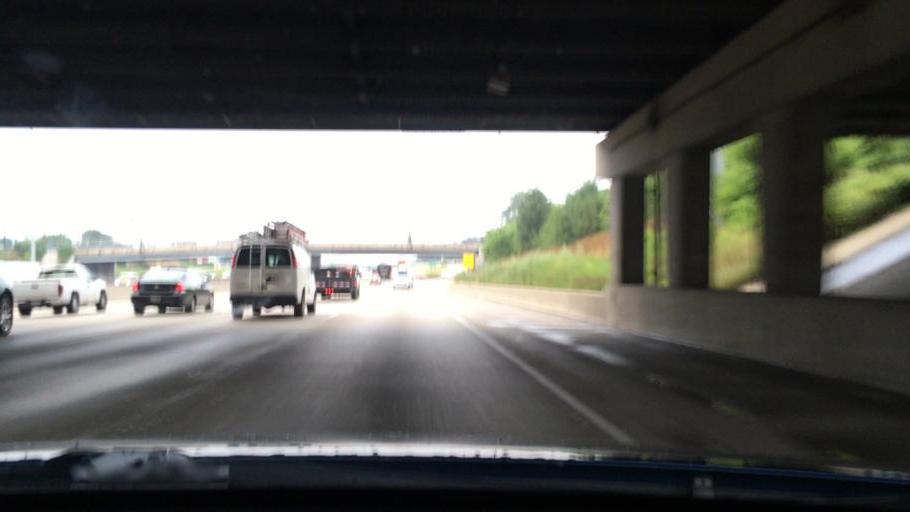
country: US
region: Illinois
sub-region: Cook County
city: Evergreen Park
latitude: 41.7582
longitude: -87.6259
